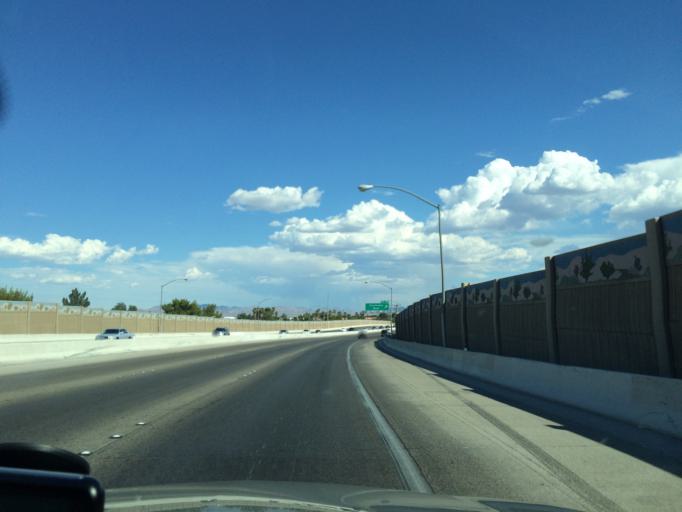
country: US
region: Nevada
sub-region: Clark County
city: North Las Vegas
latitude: 36.1647
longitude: -115.0946
